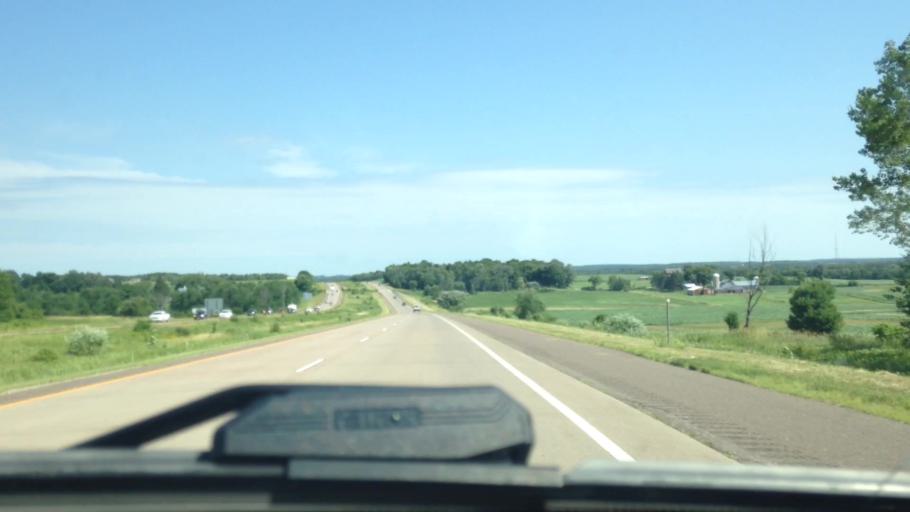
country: US
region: Wisconsin
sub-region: Barron County
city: Rice Lake
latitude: 45.5233
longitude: -91.7594
